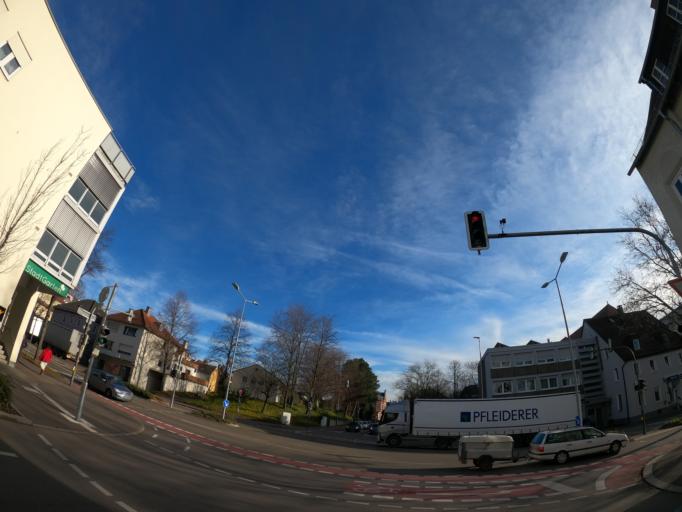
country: DE
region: Baden-Wuerttemberg
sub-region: Regierungsbezirk Stuttgart
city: Goeppingen
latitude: 48.7069
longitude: 9.6492
